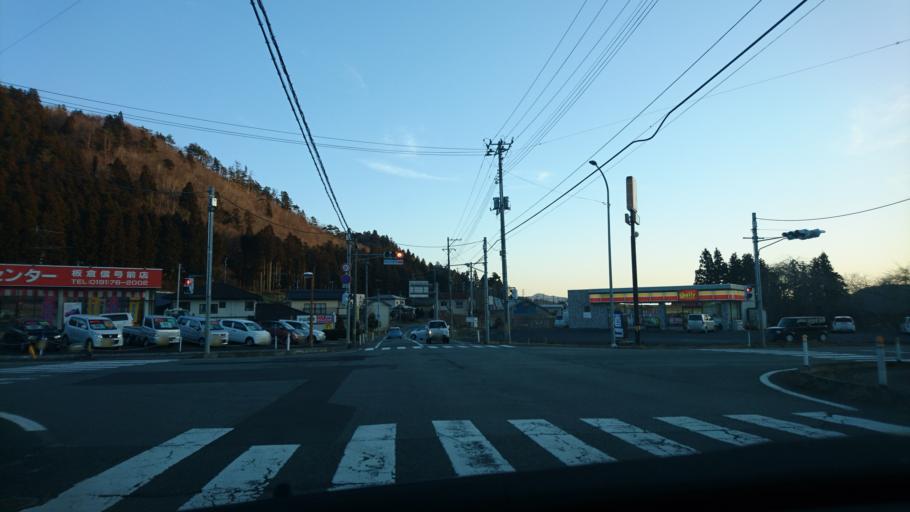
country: JP
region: Iwate
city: Mizusawa
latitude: 39.0334
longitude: 141.2952
